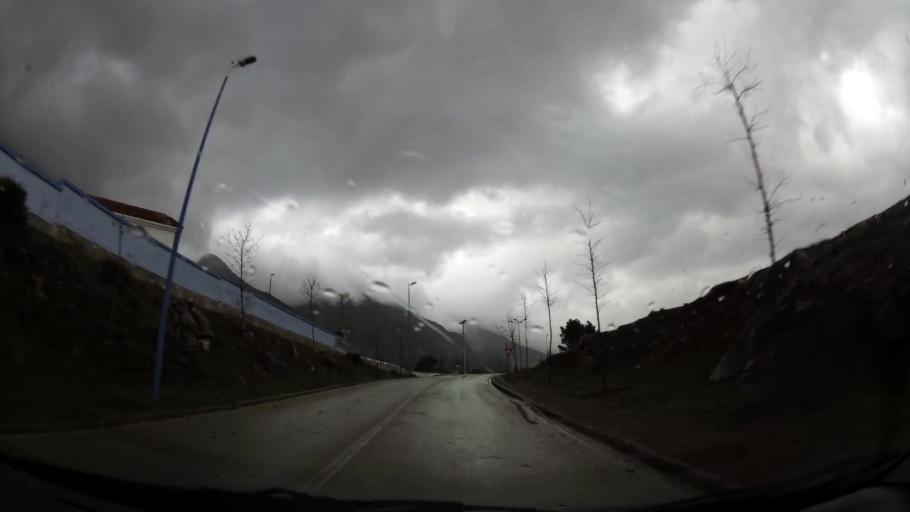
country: MA
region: Tanger-Tetouan
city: Chefchaouene
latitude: 35.1742
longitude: -5.2666
